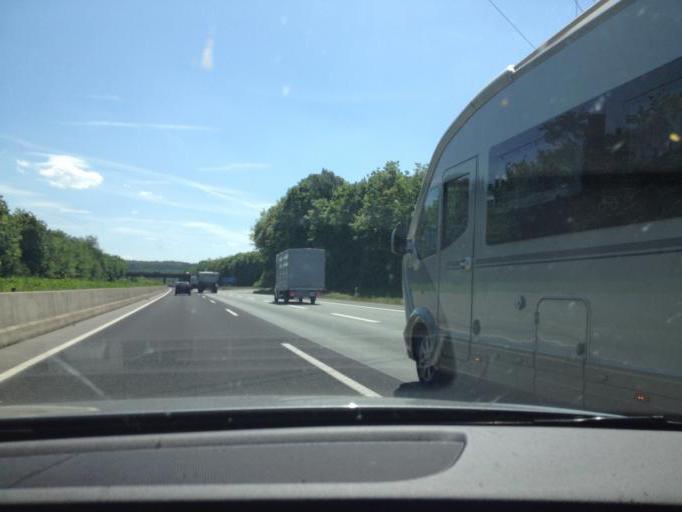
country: DE
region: North Rhine-Westphalia
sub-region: Regierungsbezirk Koln
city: Euskirchen
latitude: 50.6513
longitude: 6.7221
